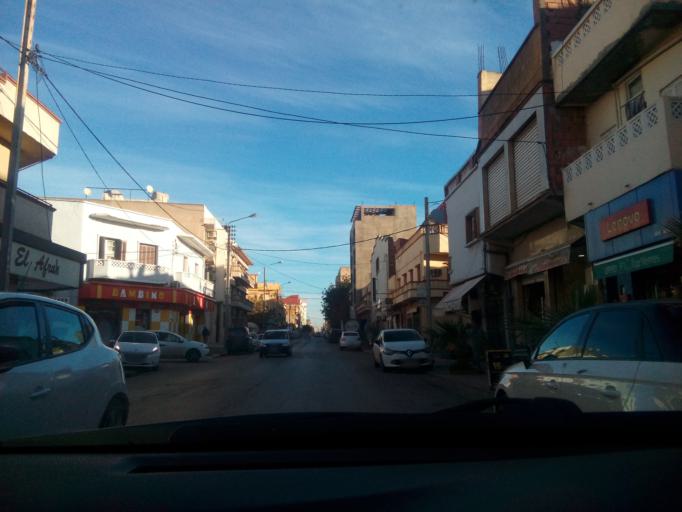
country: DZ
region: Oran
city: Oran
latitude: 35.6830
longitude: -0.6584
